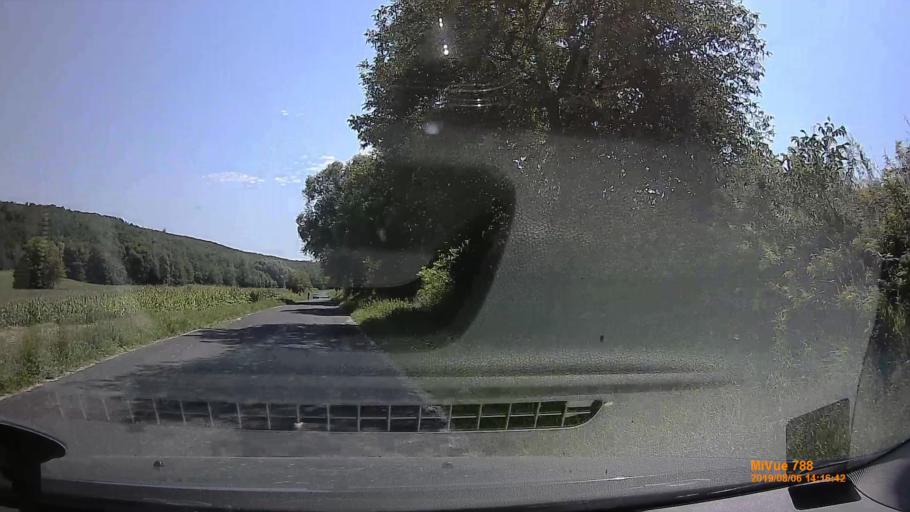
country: HU
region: Zala
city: Zalakomar
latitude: 46.5508
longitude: 17.0815
